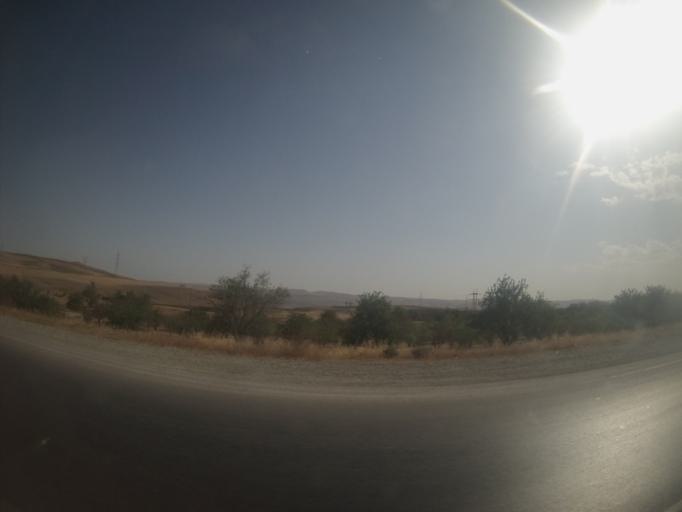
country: AZ
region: Qobustan
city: Qobustan
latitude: 40.5339
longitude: 48.7787
